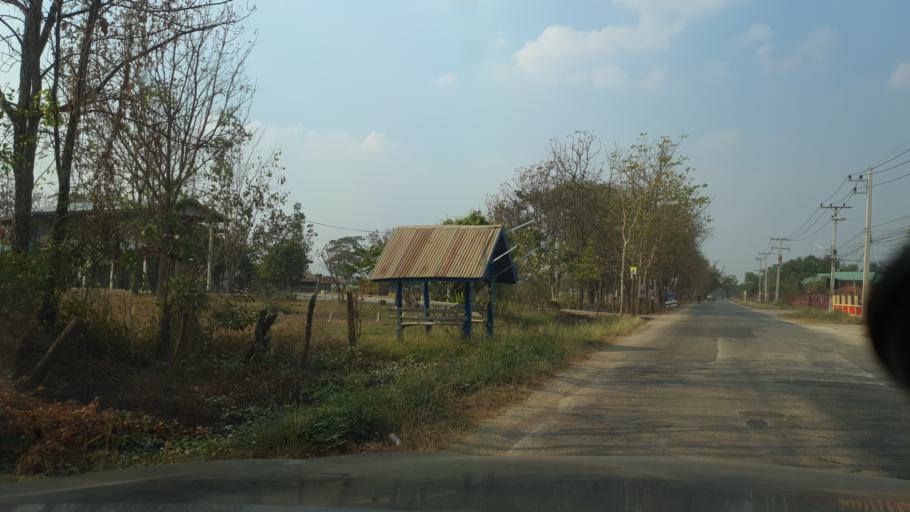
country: TH
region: Sukhothai
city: Ban Dan Lan Hoi
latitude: 17.1041
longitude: 99.5520
